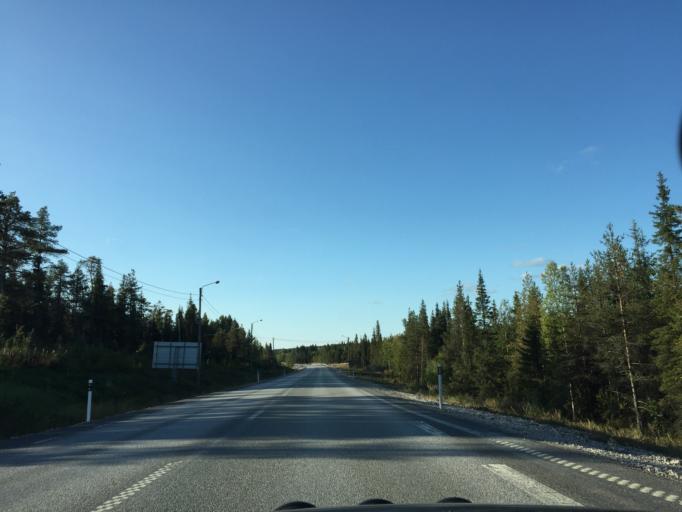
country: SE
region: Norrbotten
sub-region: Gallivare Kommun
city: Malmberget
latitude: 67.6373
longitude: 21.0649
